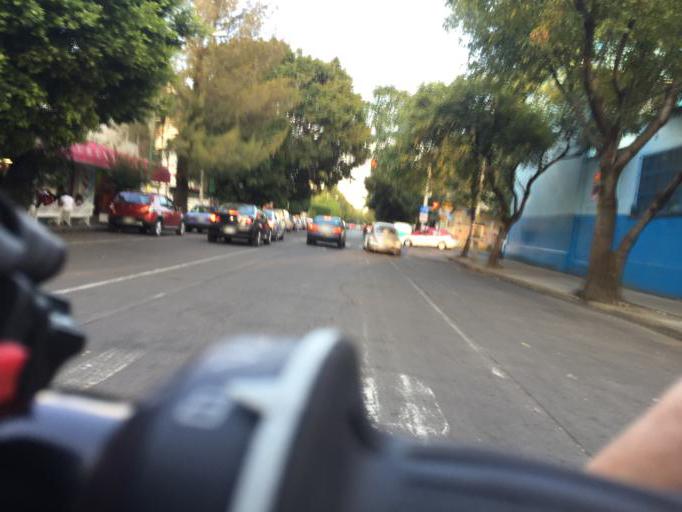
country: MX
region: Mexico City
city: Coyoacan
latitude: 19.3533
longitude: -99.1612
